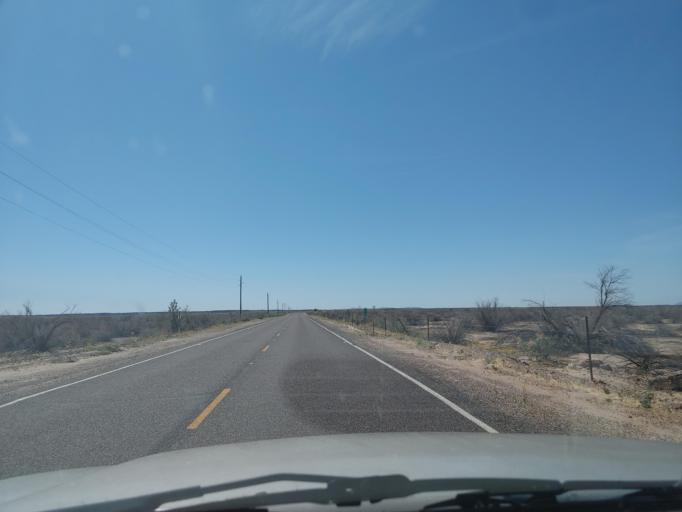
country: US
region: Arizona
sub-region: Maricopa County
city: Gila Bend
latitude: 32.9679
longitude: -113.3060
